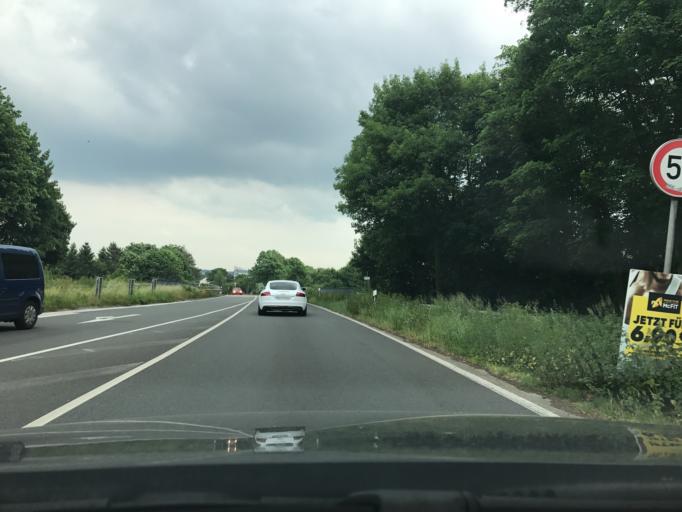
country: DE
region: North Rhine-Westphalia
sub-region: Regierungsbezirk Dusseldorf
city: Ratingen
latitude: 51.3000
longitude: 6.8061
